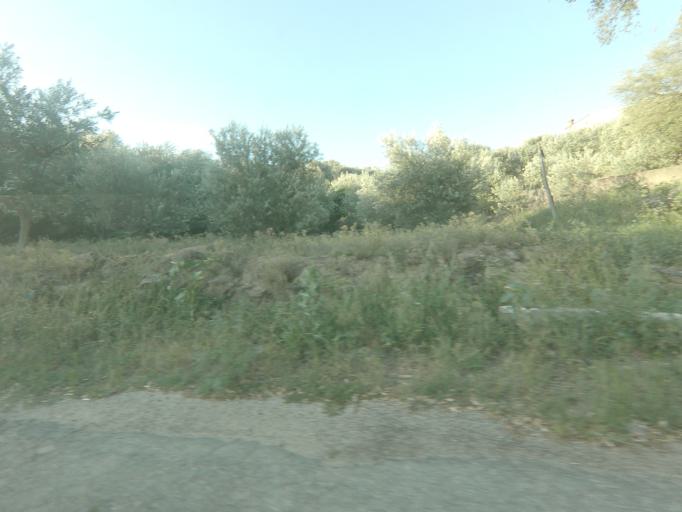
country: PT
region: Viseu
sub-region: Armamar
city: Armamar
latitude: 41.1208
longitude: -7.6679
